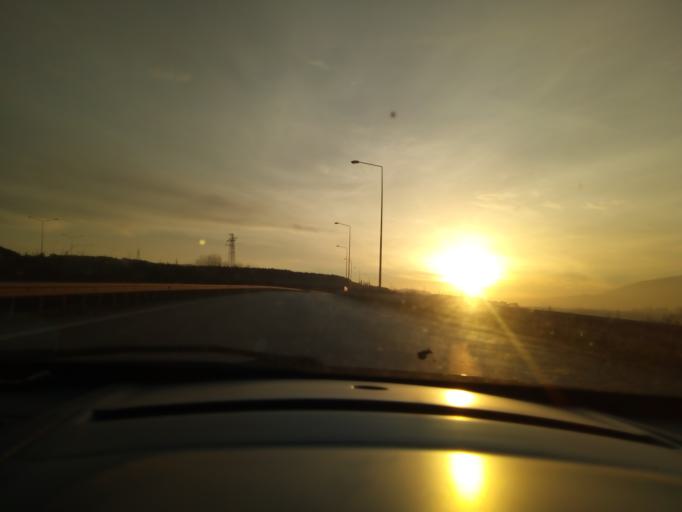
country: TR
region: Bursa
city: Niluefer
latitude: 40.2893
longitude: 29.0220
